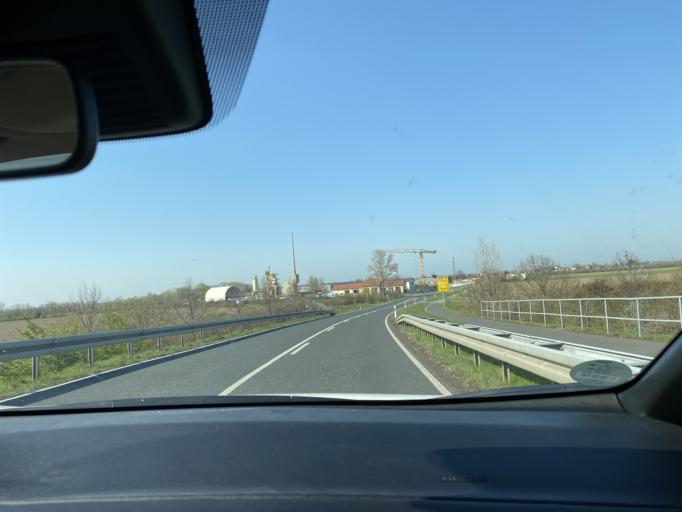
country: DE
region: Saxony
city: Zwenkau
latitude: 51.2591
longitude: 12.2862
